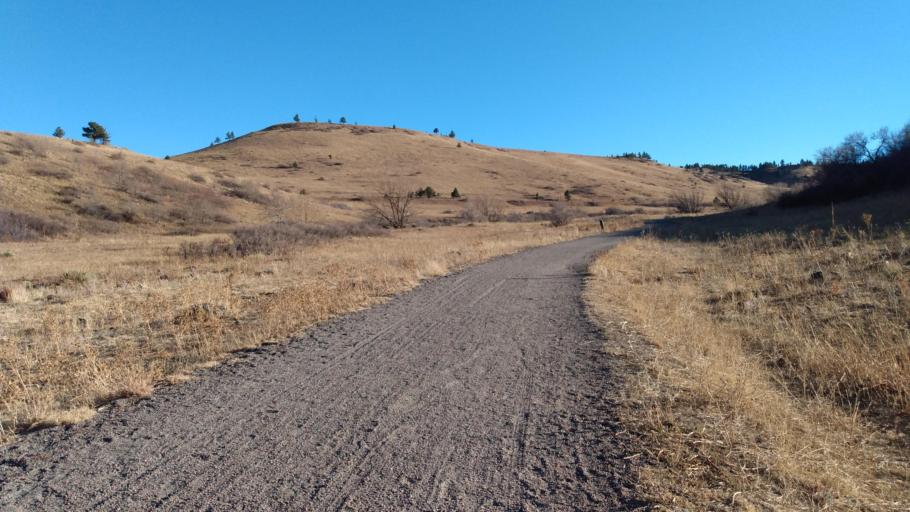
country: US
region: Colorado
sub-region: Boulder County
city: Boulder
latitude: 39.9367
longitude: -105.2561
